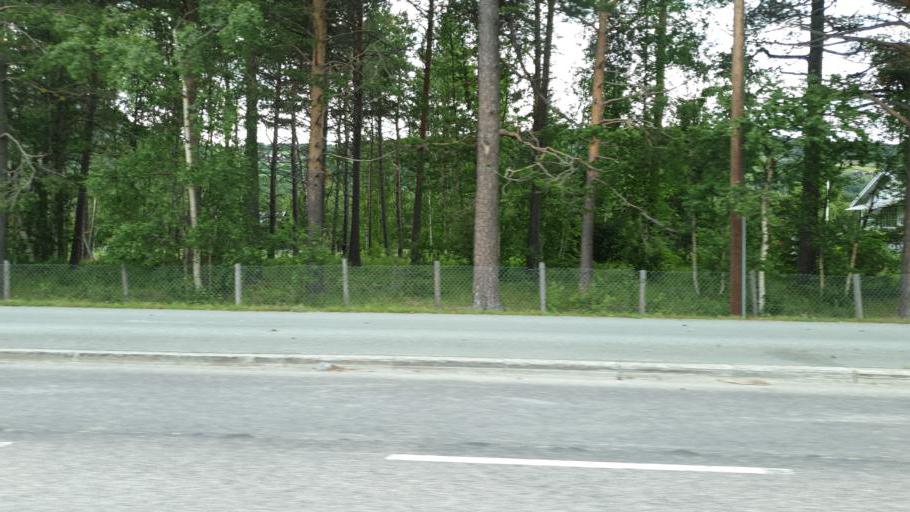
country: NO
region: Sor-Trondelag
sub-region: Oppdal
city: Oppdal
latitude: 62.5661
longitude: 9.6453
